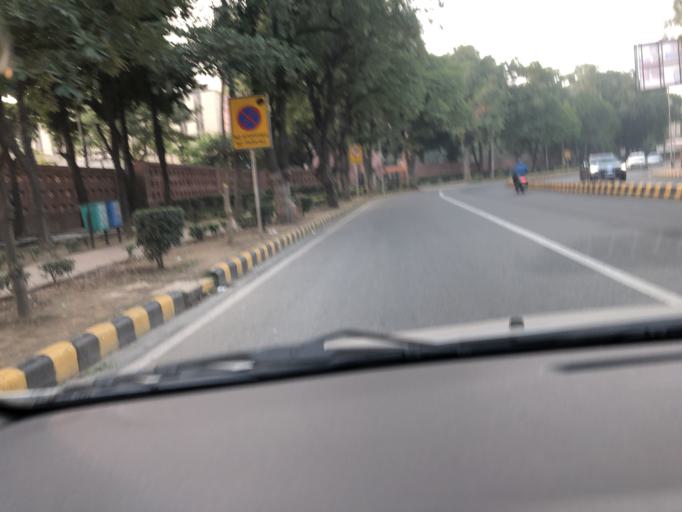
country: IN
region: NCT
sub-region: New Delhi
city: New Delhi
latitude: 28.6205
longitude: 77.2101
